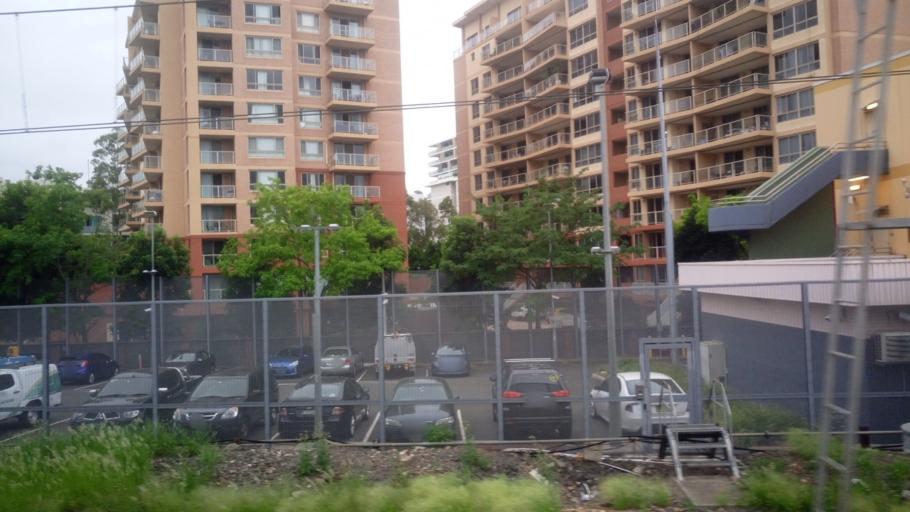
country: AU
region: New South Wales
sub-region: Strathfield
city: Homebush
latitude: -33.8670
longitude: 151.0873
